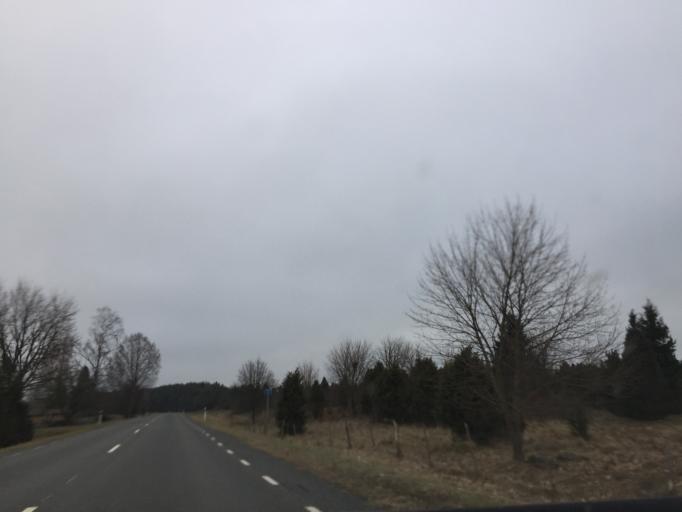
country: EE
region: Saare
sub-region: Kuressaare linn
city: Kuressaare
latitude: 58.5402
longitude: 22.3378
